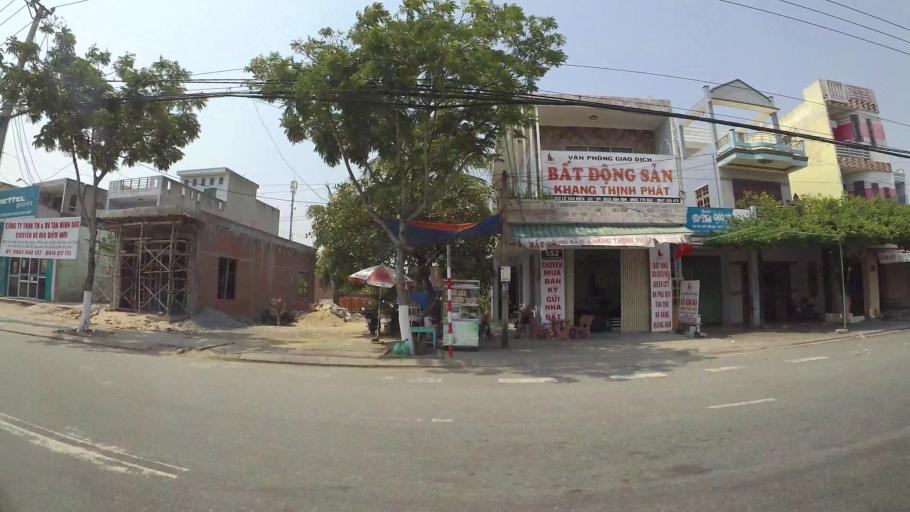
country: VN
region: Da Nang
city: Ngu Hanh Son
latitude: 16.0100
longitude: 108.2571
